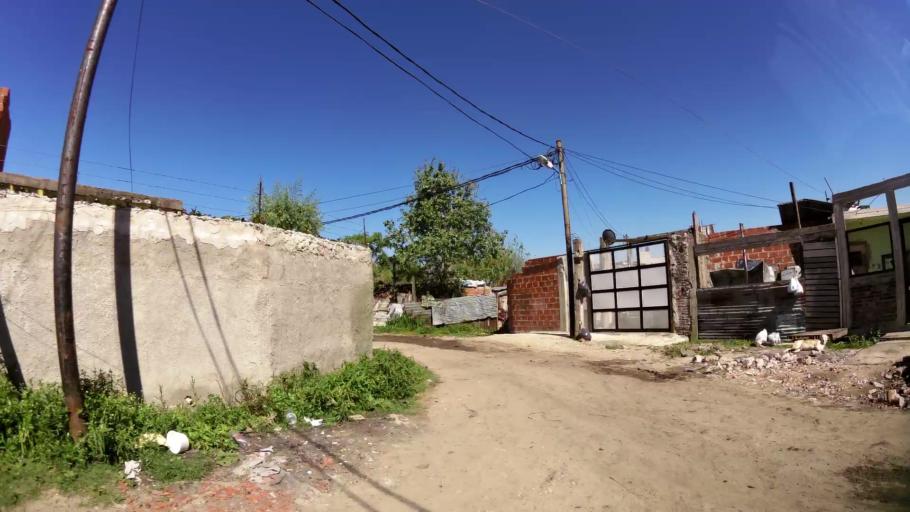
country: AR
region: Buenos Aires
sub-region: Partido de Quilmes
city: Quilmes
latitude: -34.7074
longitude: -58.3037
